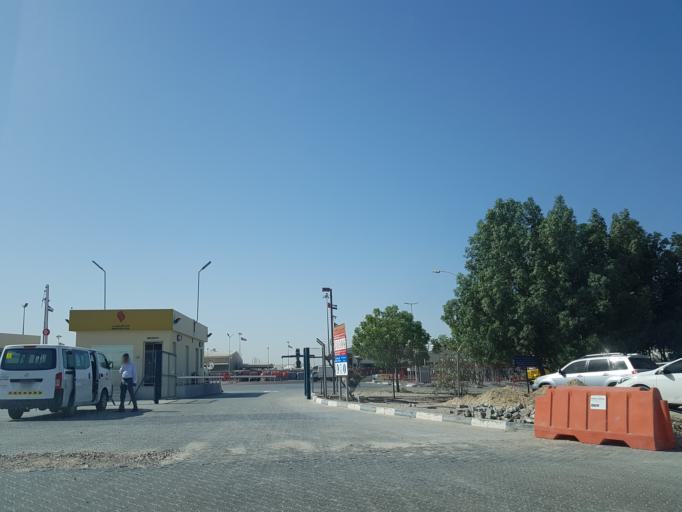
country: AE
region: Dubai
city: Dubai
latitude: 25.0174
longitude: 55.0862
